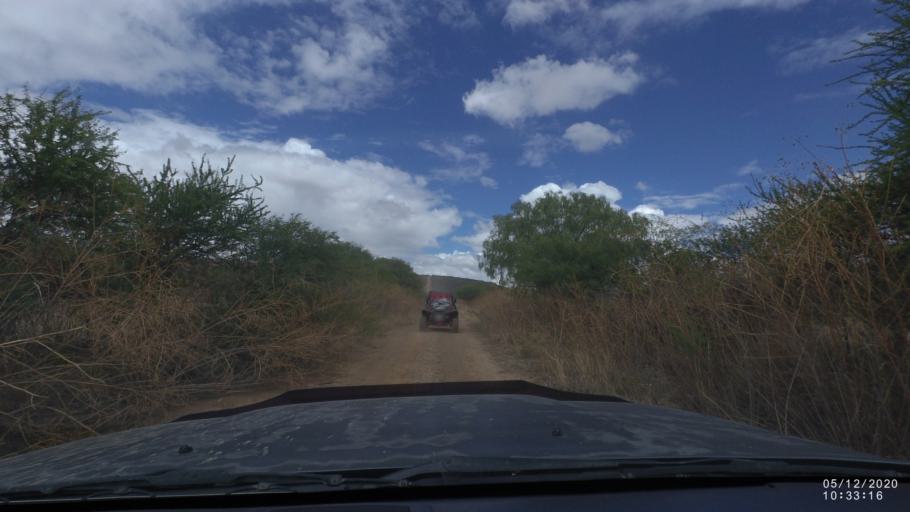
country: BO
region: Cochabamba
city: Sipe Sipe
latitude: -17.5458
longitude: -66.2722
